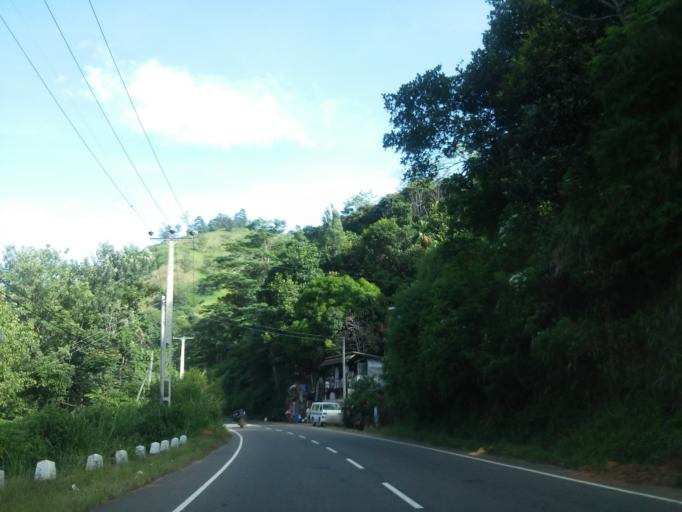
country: LK
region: Uva
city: Haputale
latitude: 6.7639
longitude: 80.8993
